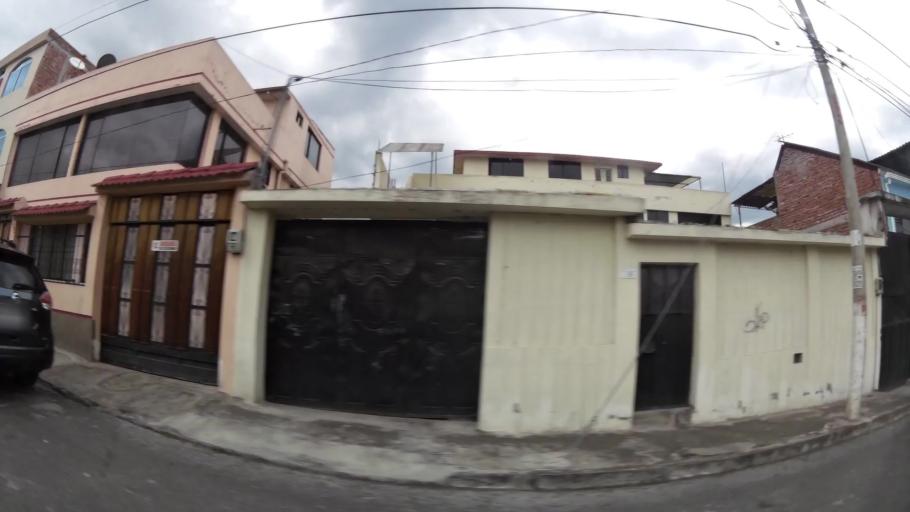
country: EC
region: Tungurahua
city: Ambato
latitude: -1.2305
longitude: -78.6222
